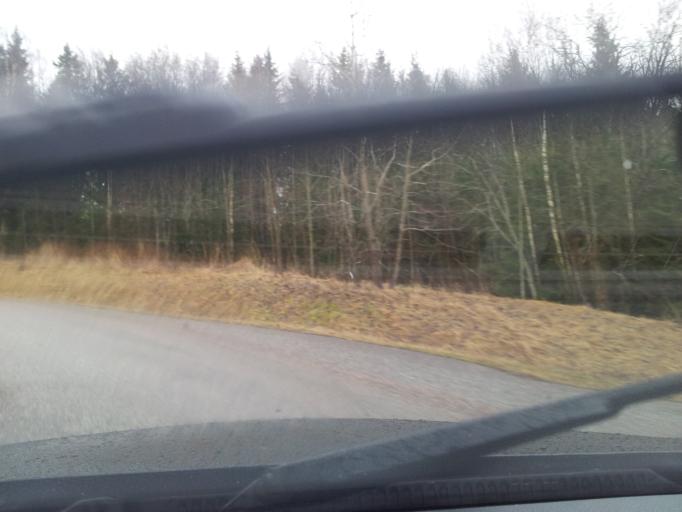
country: FI
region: Uusimaa
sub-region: Helsinki
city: Kirkkonummi
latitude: 60.1610
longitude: 24.5434
